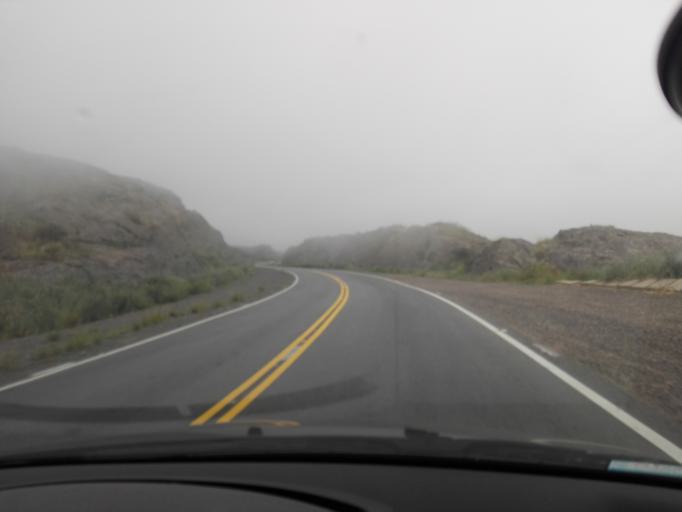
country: AR
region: Cordoba
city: Cuesta Blanca
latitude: -31.5975
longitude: -64.7099
